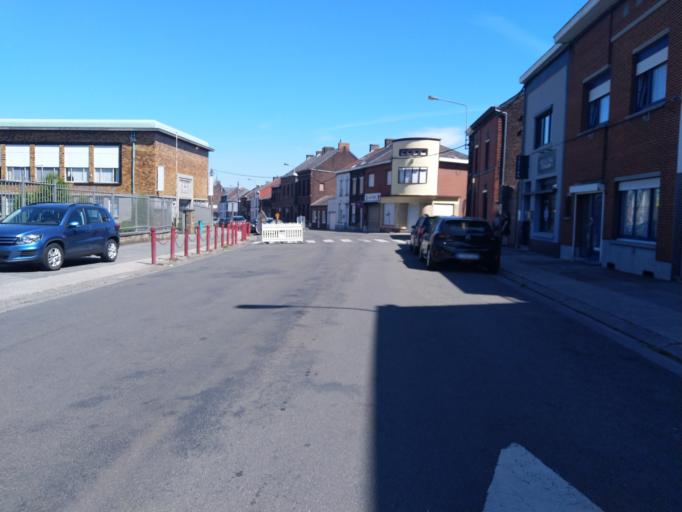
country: BE
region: Wallonia
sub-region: Province du Hainaut
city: Colfontaine
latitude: 50.4062
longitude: 3.8634
